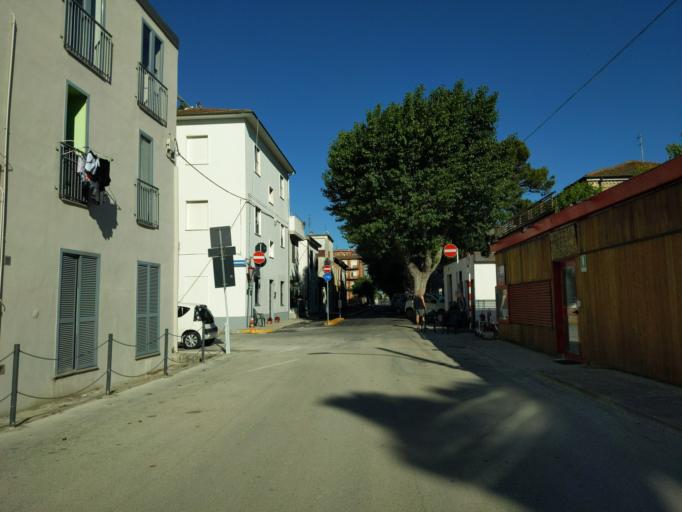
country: IT
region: The Marches
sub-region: Provincia di Ancona
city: Falconara Marittima
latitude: 43.6382
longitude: 13.3726
